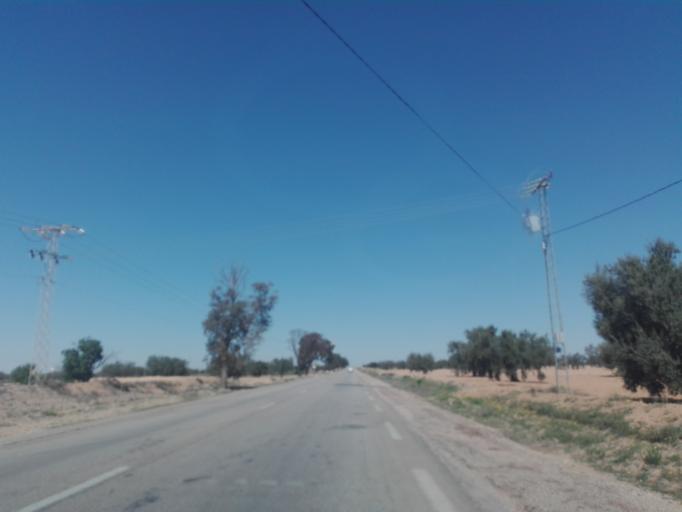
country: TN
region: Safaqis
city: Bi'r `Ali Bin Khalifah
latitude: 34.7534
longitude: 10.3379
